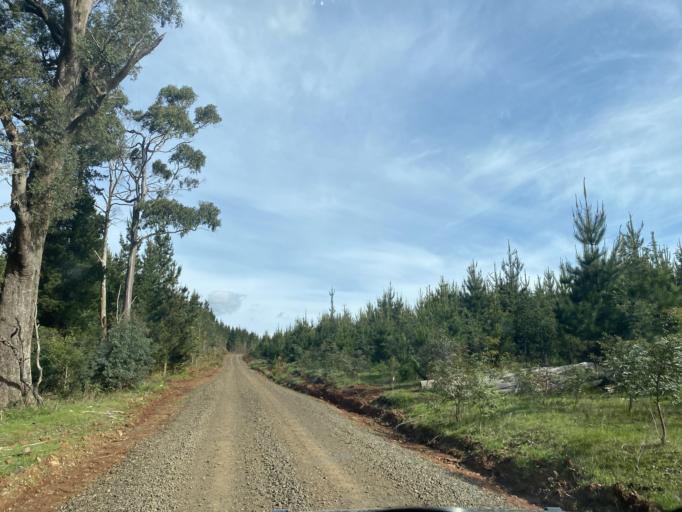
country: AU
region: Victoria
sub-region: Mansfield
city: Mansfield
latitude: -36.8307
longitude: 146.1791
